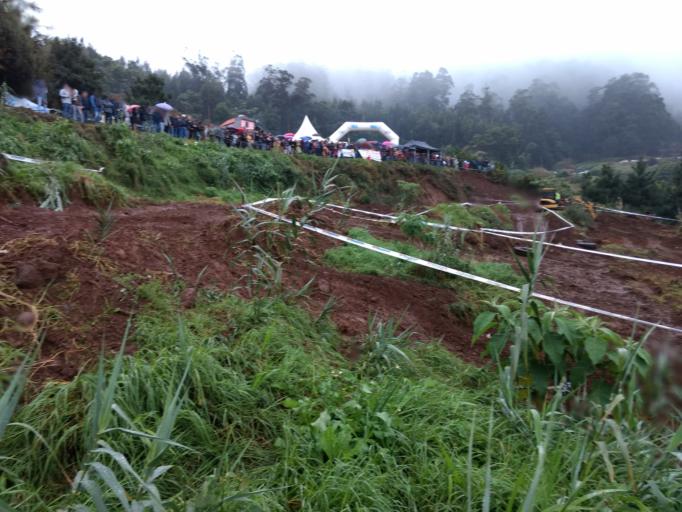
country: PT
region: Madeira
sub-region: Porto Moniz
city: Porto Moniz
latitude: 32.8528
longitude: -17.1669
